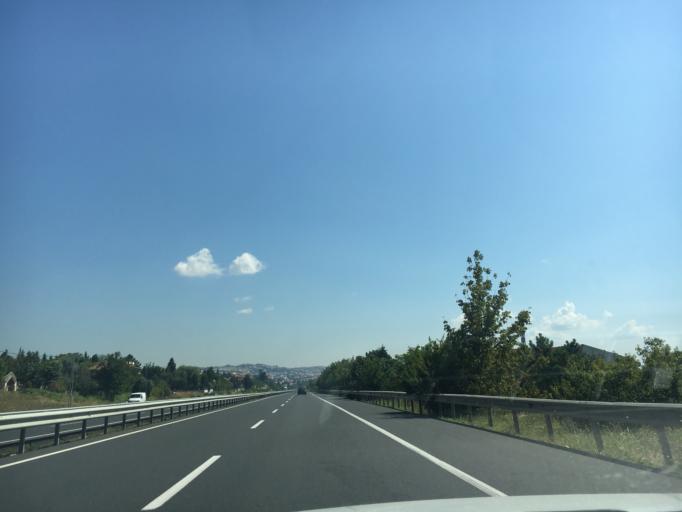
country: TR
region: Tekirdag
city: Sultankoy
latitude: 41.0288
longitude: 28.0035
